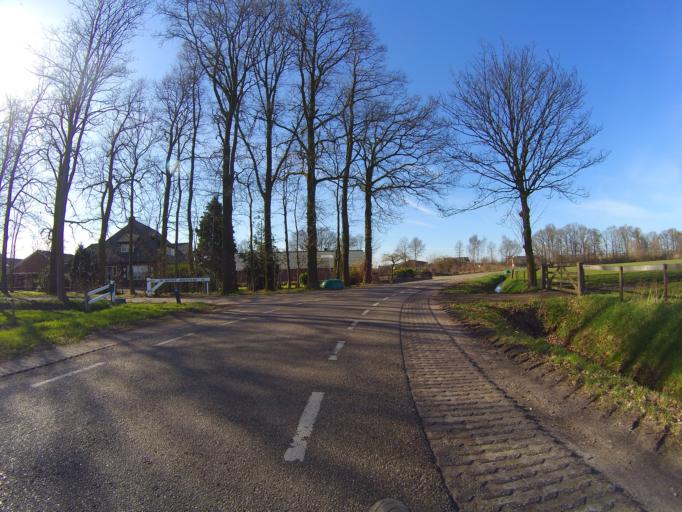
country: NL
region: Utrecht
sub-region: Gemeente Utrechtse Heuvelrug
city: Overberg
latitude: 52.0657
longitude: 5.5160
